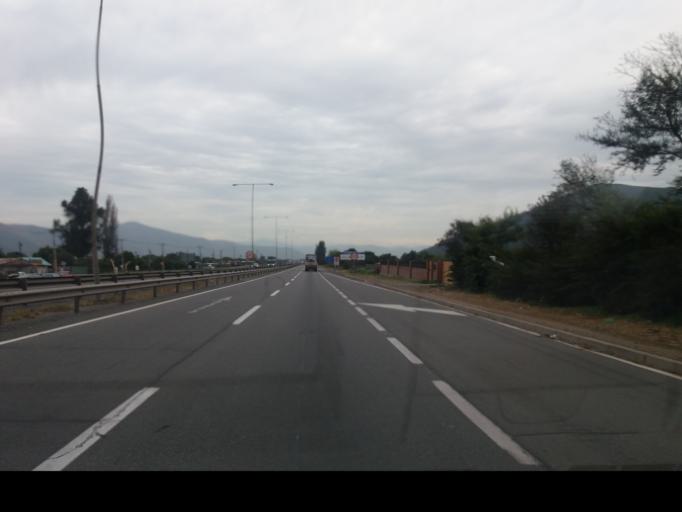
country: CL
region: Valparaiso
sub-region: Provincia de Quillota
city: Hacienda La Calera
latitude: -32.8398
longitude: -71.1121
